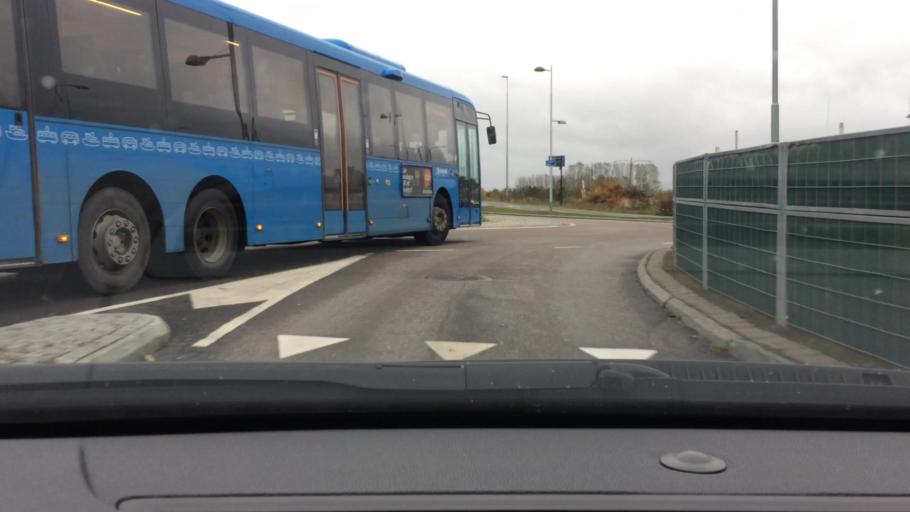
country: SE
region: Vaestra Goetaland
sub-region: Goteborg
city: Eriksbo
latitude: 57.7337
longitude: 12.0294
